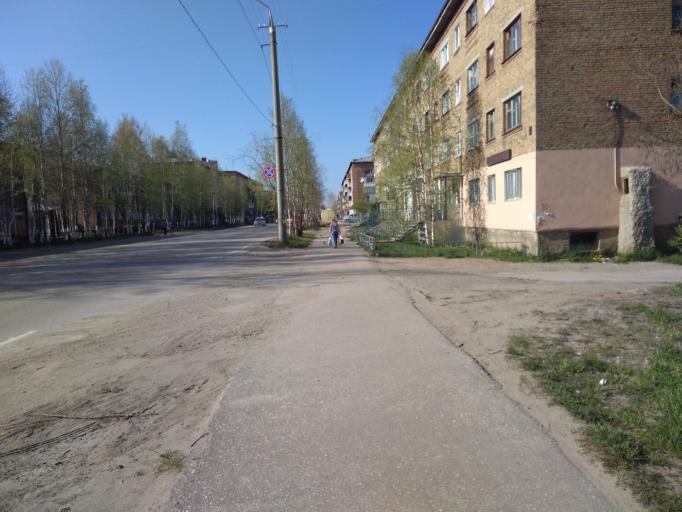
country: RU
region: Komi Republic
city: Pechora
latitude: 65.1228
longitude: 57.1543
